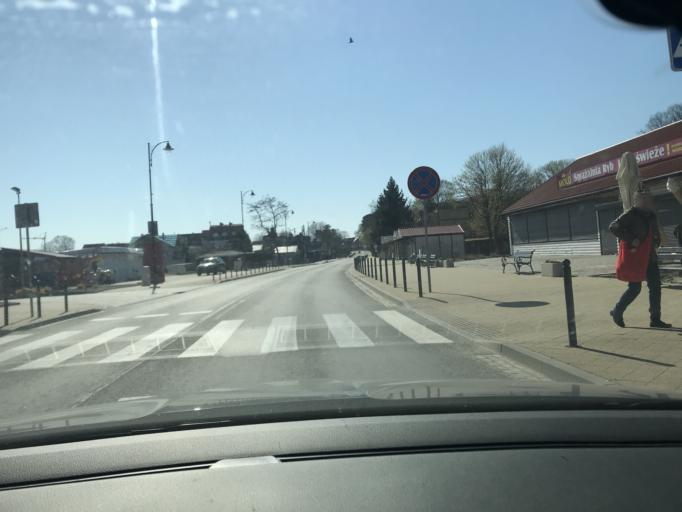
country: PL
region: Pomeranian Voivodeship
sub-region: Powiat nowodworski
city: Krynica Morska
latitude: 54.3792
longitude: 19.4419
